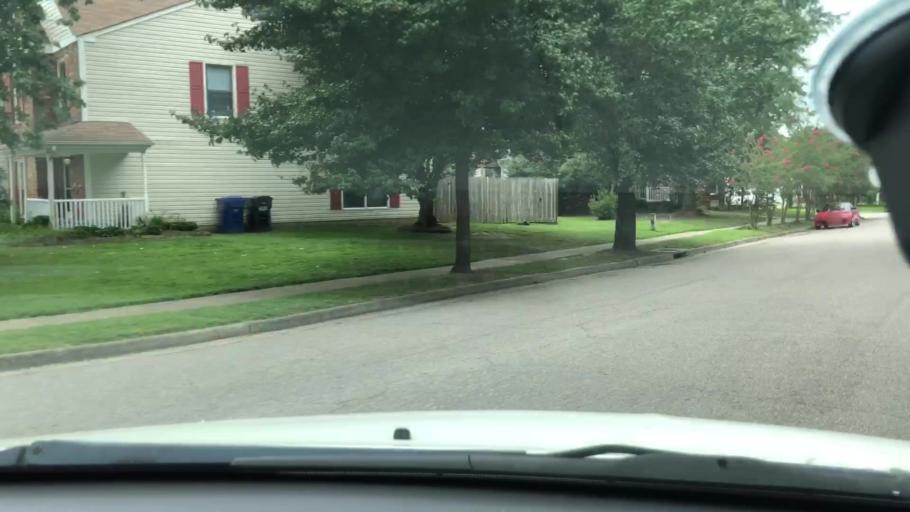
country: US
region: Virginia
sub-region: City of Virginia Beach
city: Virginia Beach
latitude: 36.8448
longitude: -76.1148
